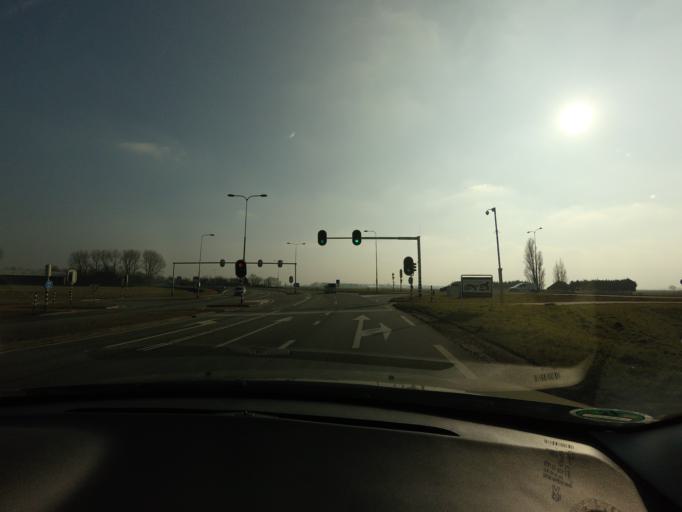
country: NL
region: North Holland
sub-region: Gemeente Alkmaar
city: Alkmaar
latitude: 52.6203
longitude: 4.7824
